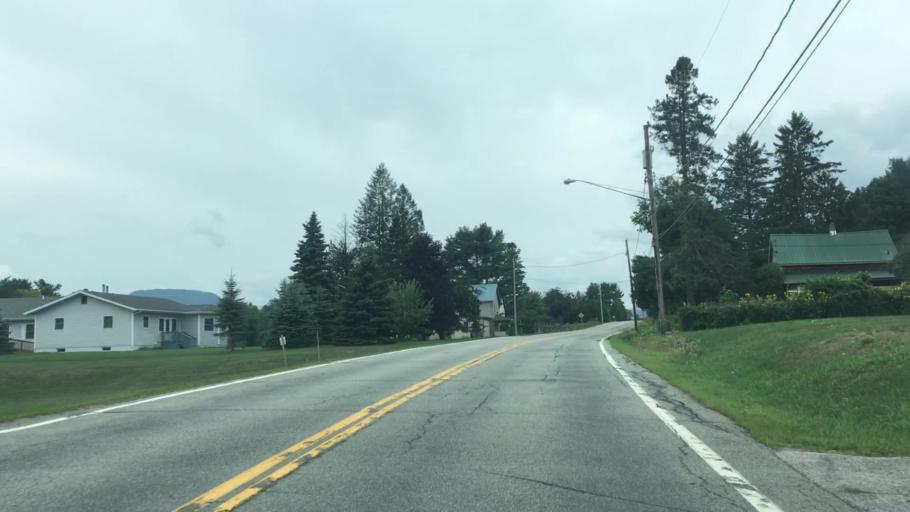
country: US
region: New York
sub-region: Essex County
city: Elizabethtown
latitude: 44.3842
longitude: -73.7148
